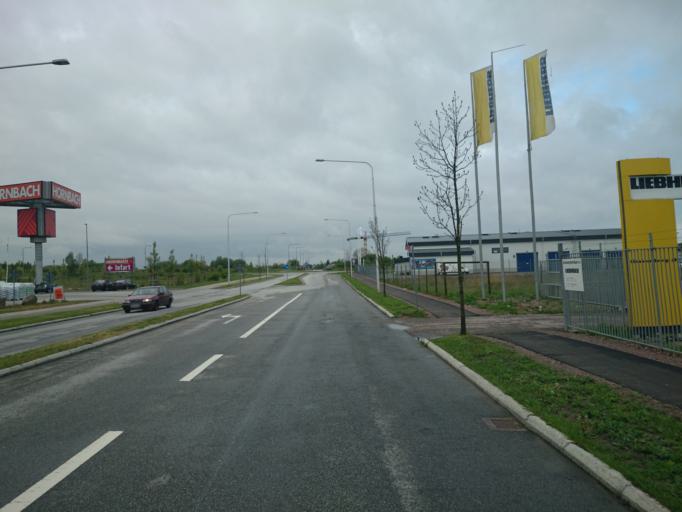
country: SE
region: Skane
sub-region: Burlovs Kommun
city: Arloev
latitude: 55.6119
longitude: 13.0941
